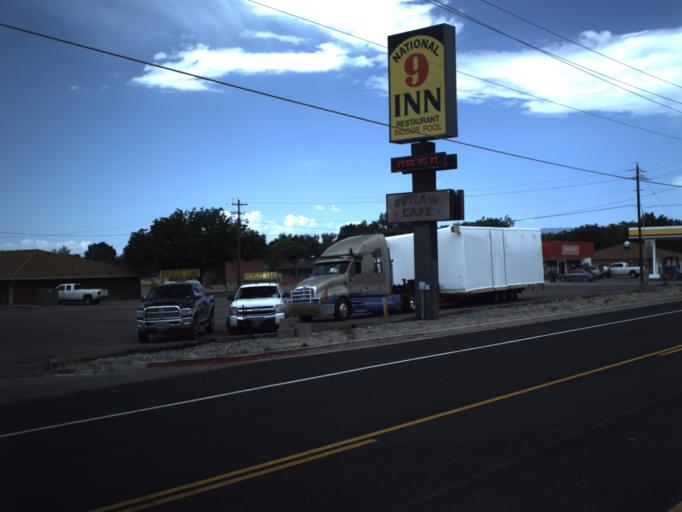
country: US
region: Utah
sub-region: Carbon County
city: Wellington
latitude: 39.5425
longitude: -110.7228
